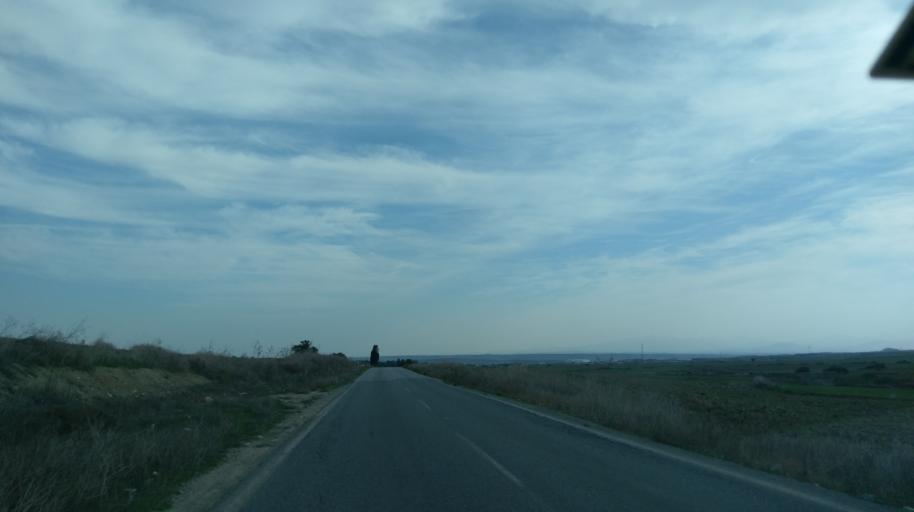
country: CY
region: Lefkosia
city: Mammari
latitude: 35.2441
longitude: 33.1550
